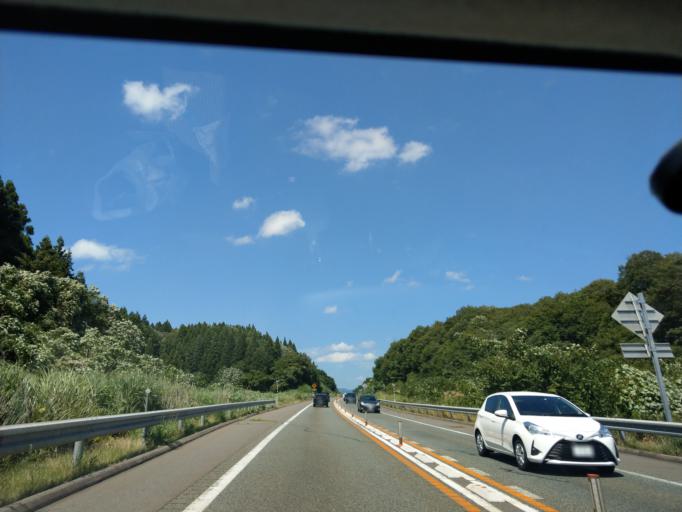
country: JP
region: Akita
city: Akita
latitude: 39.6787
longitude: 140.1857
